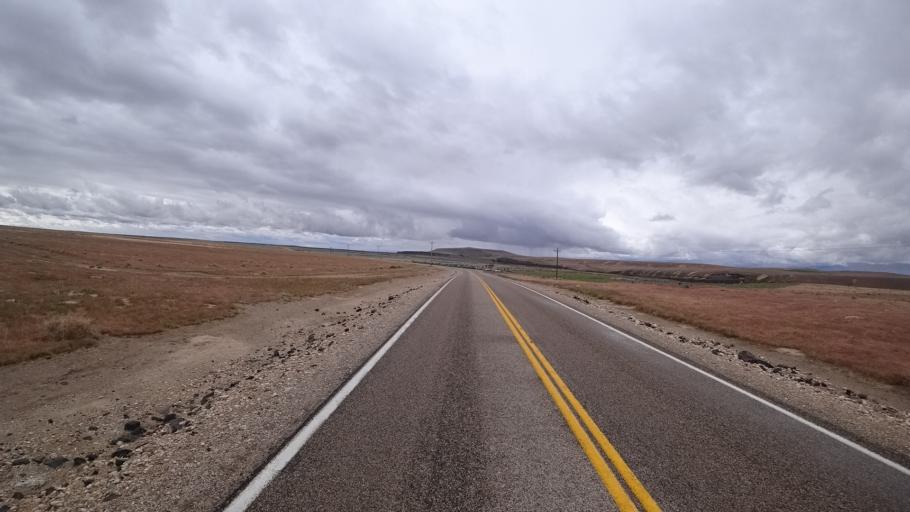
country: US
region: Idaho
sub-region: Owyhee County
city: Murphy
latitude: 43.2783
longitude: -116.3943
